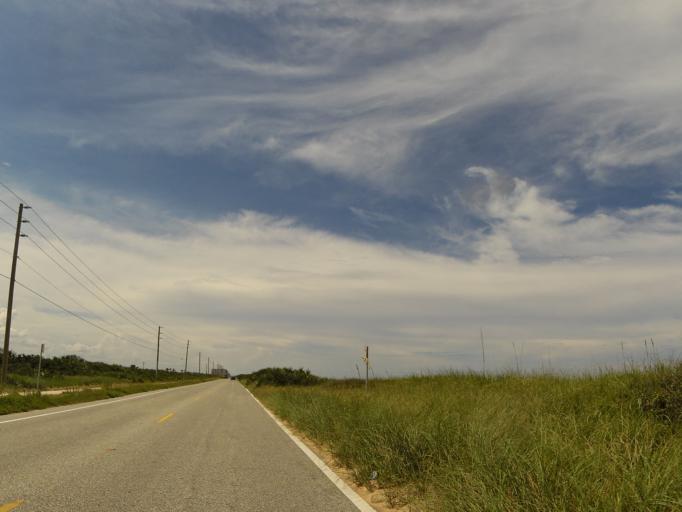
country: US
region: Florida
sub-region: Flagler County
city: Flagler Beach
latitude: 29.4146
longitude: -81.0970
